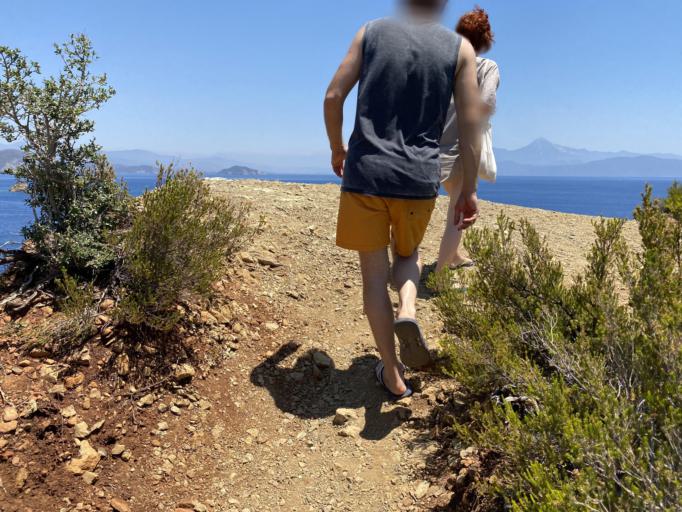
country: TR
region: Mugla
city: Goecek
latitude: 36.7066
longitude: 28.9348
